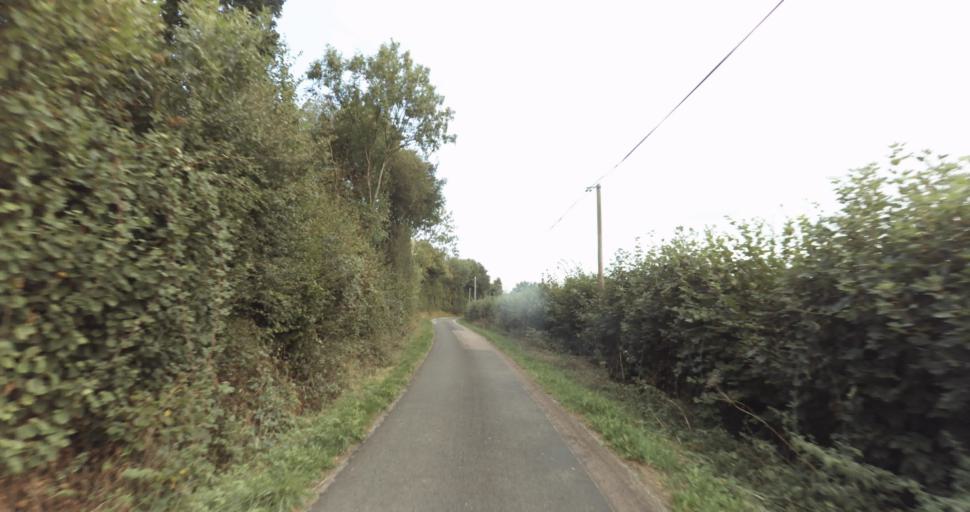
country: FR
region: Lower Normandy
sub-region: Departement de l'Orne
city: Gace
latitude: 48.7664
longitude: 0.3549
